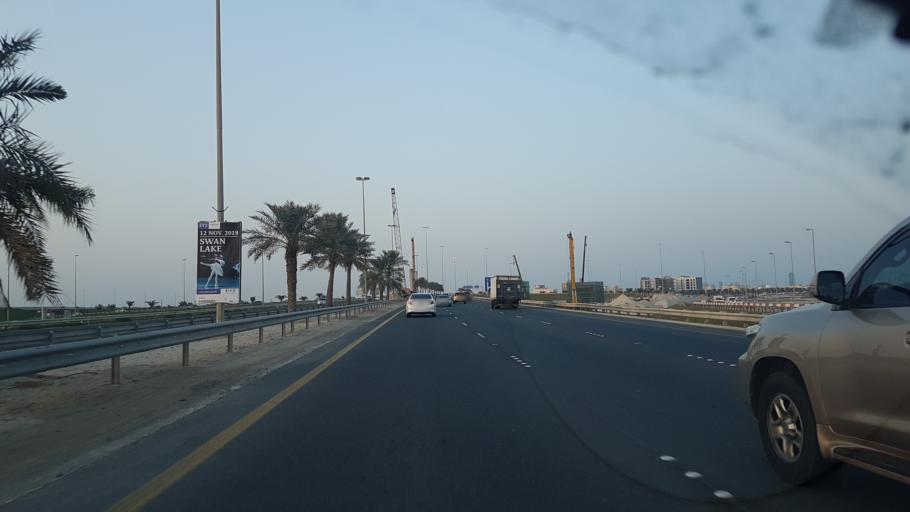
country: BH
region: Northern
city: Madinat `Isa
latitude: 26.1801
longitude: 50.5025
